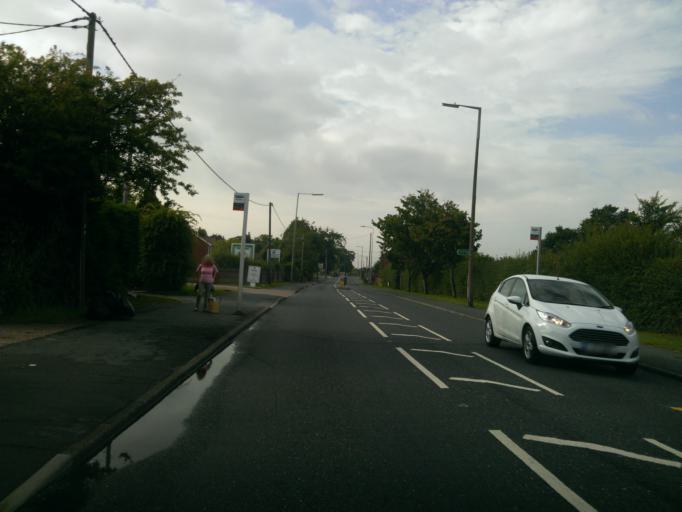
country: GB
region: England
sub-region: Essex
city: Little Clacton
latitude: 51.8240
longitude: 1.1419
